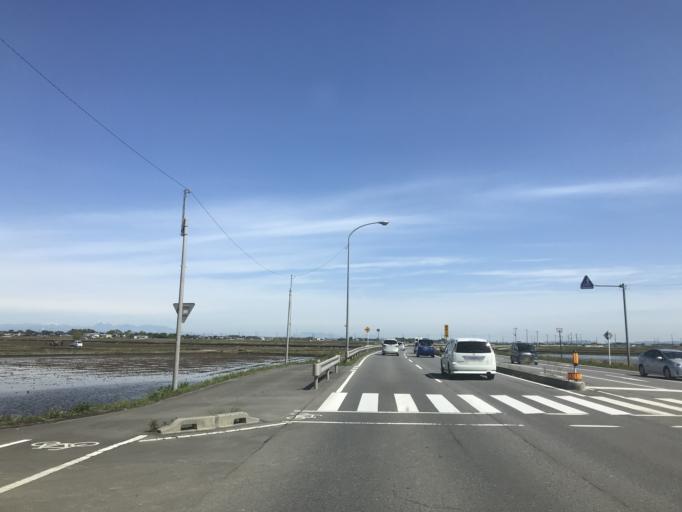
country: JP
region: Ibaraki
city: Ishige
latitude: 36.1260
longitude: 139.9820
